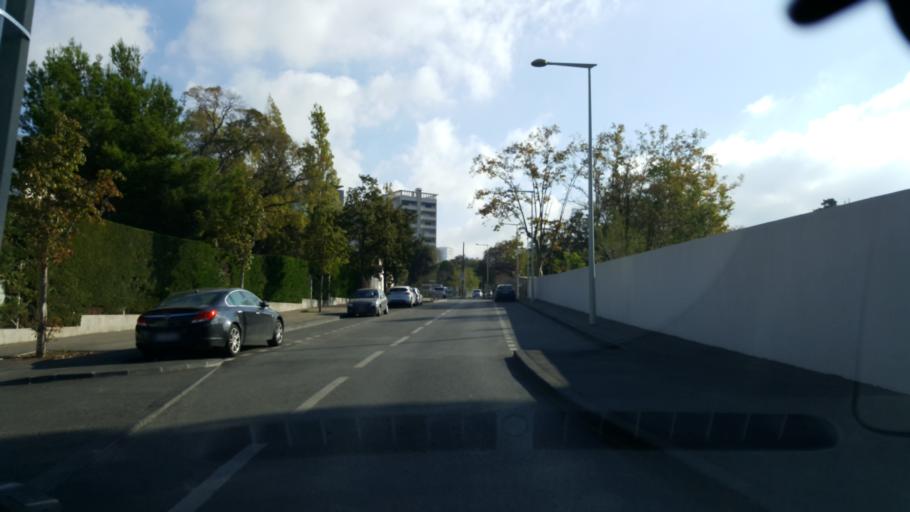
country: FR
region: Provence-Alpes-Cote d'Azur
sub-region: Departement des Bouches-du-Rhone
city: Marseille 09
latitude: 43.2630
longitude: 5.4159
